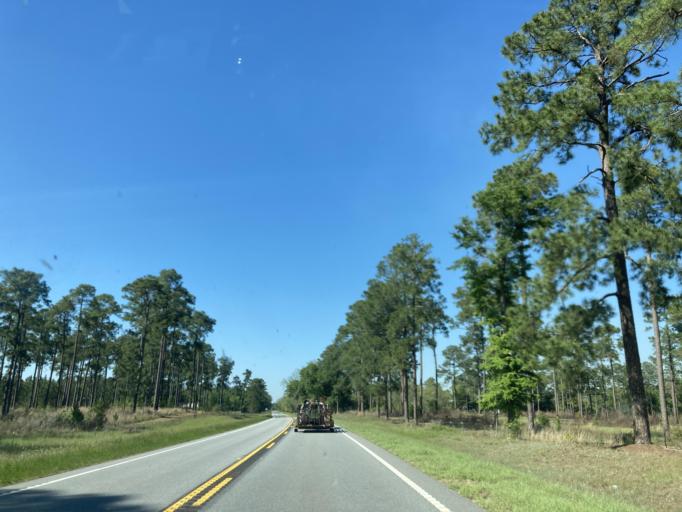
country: US
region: Georgia
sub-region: Baker County
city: Newton
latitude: 31.3984
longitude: -84.2767
